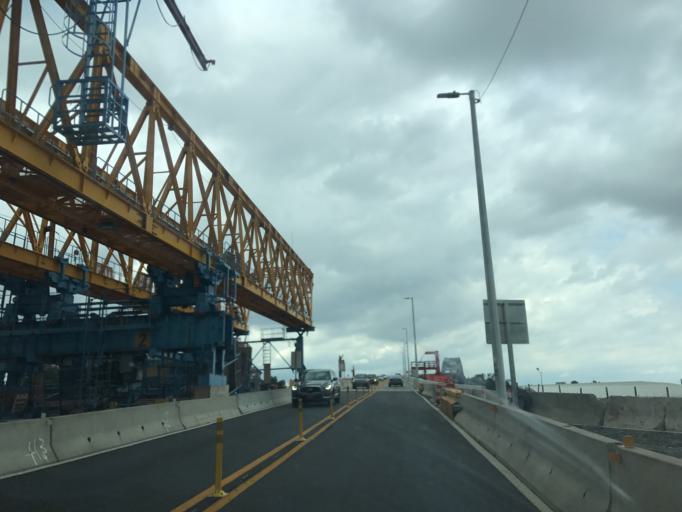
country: US
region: New York
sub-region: Richmond County
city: Bloomfield
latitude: 40.6315
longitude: -74.1456
